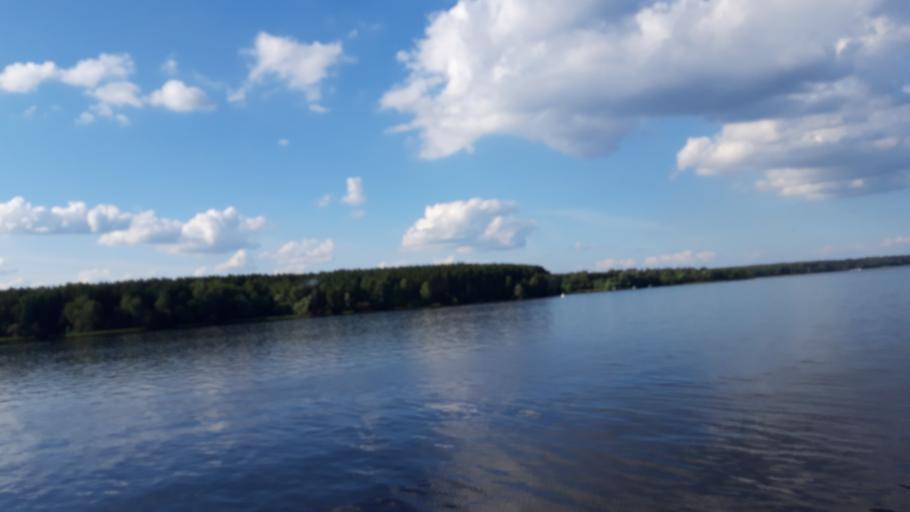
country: RU
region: Tverskaya
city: Konakovo
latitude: 56.6980
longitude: 36.7114
